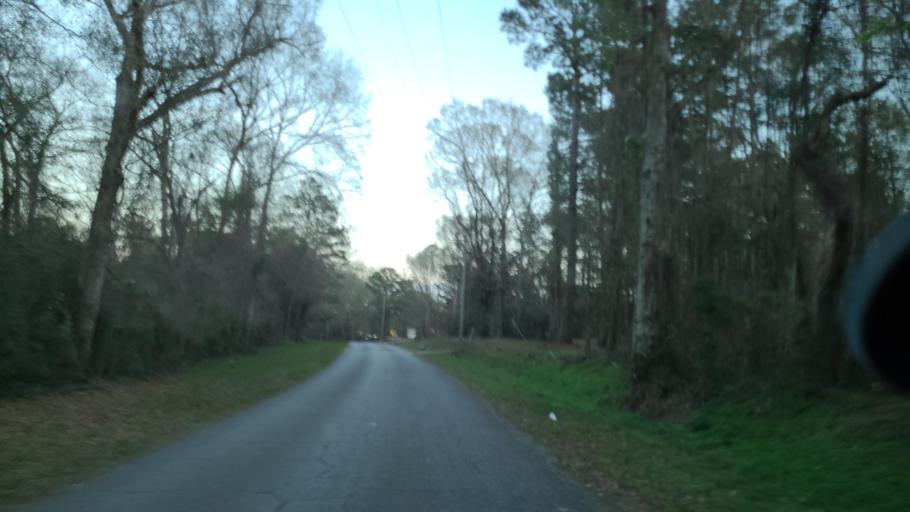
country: US
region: Mississippi
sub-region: Forrest County
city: Hattiesburg
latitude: 31.1661
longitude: -89.2122
